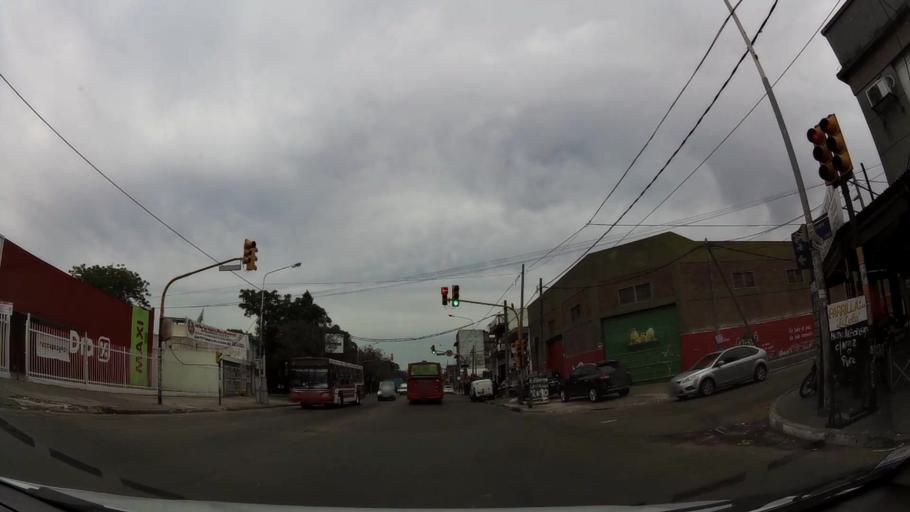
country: AR
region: Buenos Aires
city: San Justo
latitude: -34.6879
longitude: -58.5227
